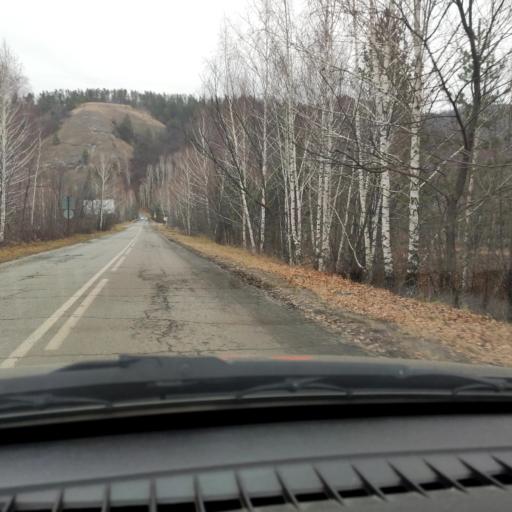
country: RU
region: Samara
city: Zhigulevsk
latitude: 53.4300
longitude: 49.6682
